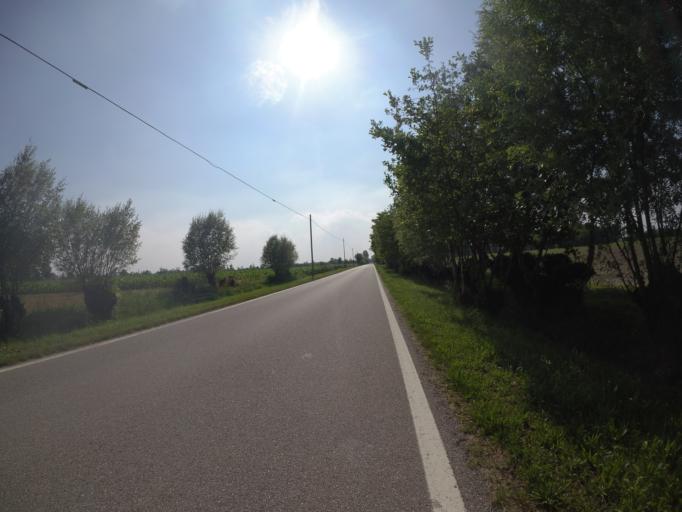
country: IT
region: Friuli Venezia Giulia
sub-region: Provincia di Udine
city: Varmo
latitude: 45.9193
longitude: 12.9839
